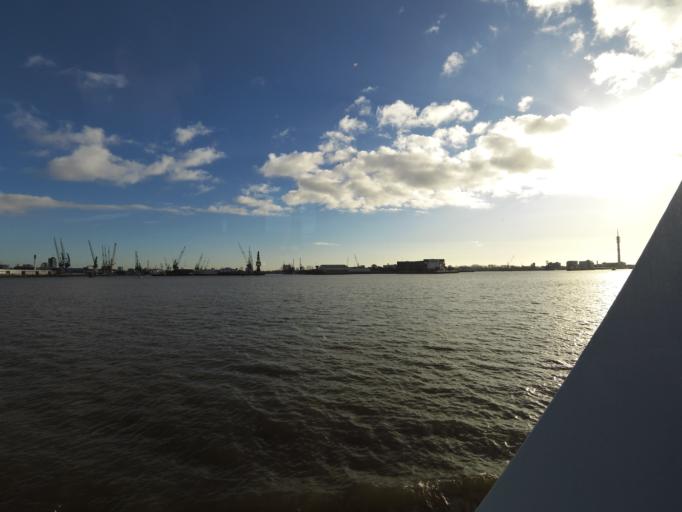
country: NL
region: South Holland
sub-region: Gemeente Rotterdam
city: Delfshaven
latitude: 51.8941
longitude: 4.4382
